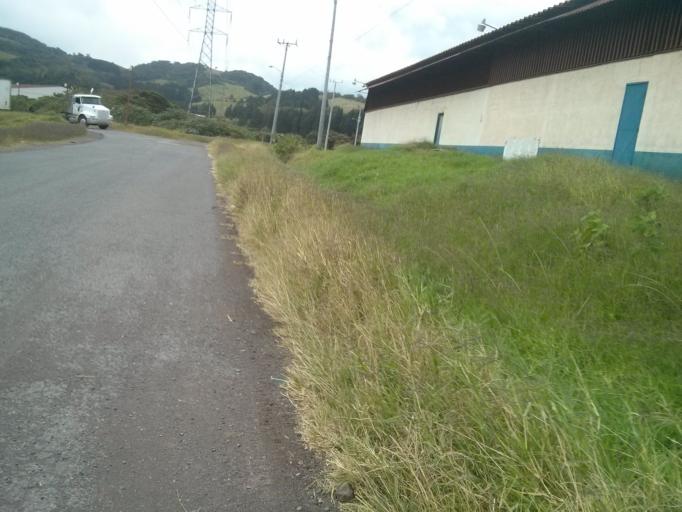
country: CR
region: Cartago
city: Cartago
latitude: 9.8929
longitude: -83.9431
